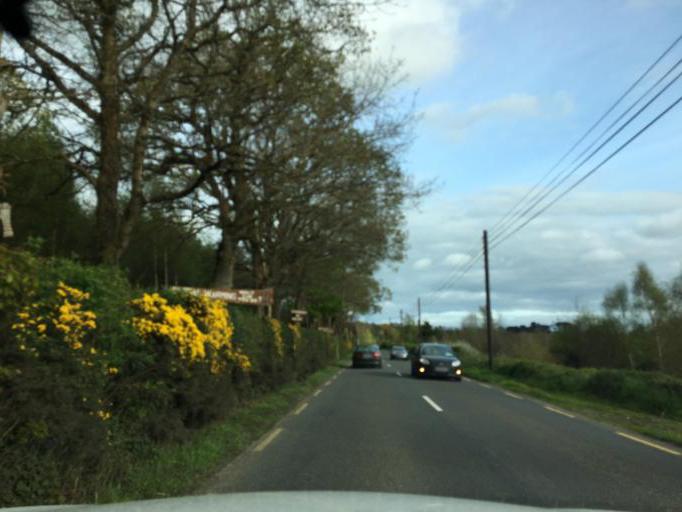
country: IE
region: Leinster
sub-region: Loch Garman
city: New Ross
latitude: 52.4239
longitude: -6.9382
